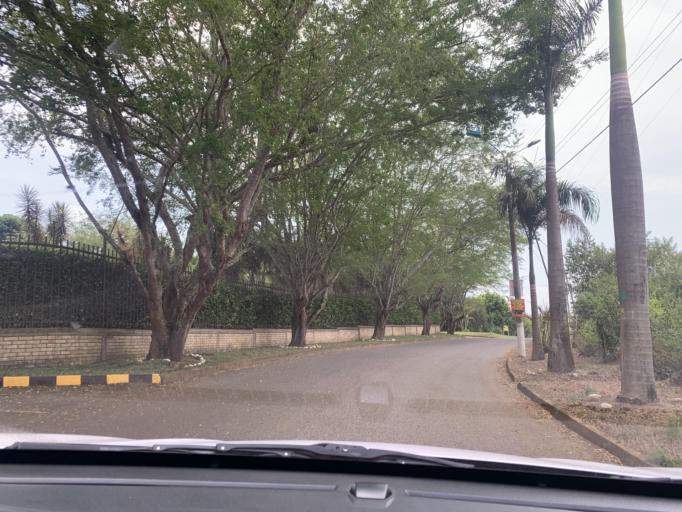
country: CO
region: Valle del Cauca
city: Jamundi
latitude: 3.3393
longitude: -76.5538
